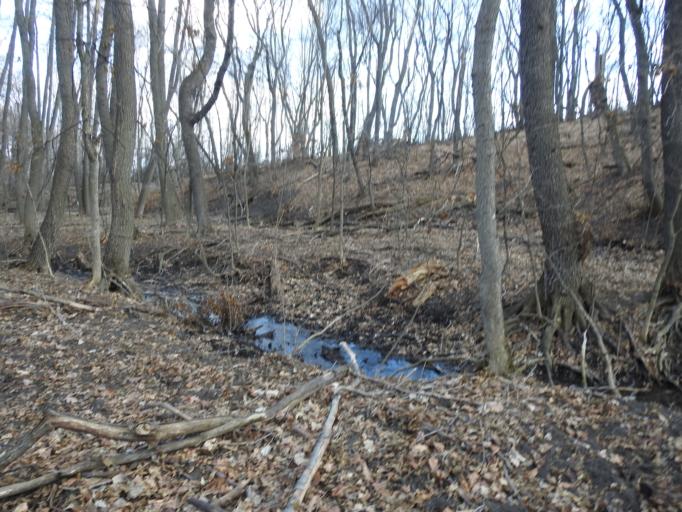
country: RU
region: Saratov
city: Krasnyy Oktyabr'
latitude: 51.3834
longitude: 45.7782
